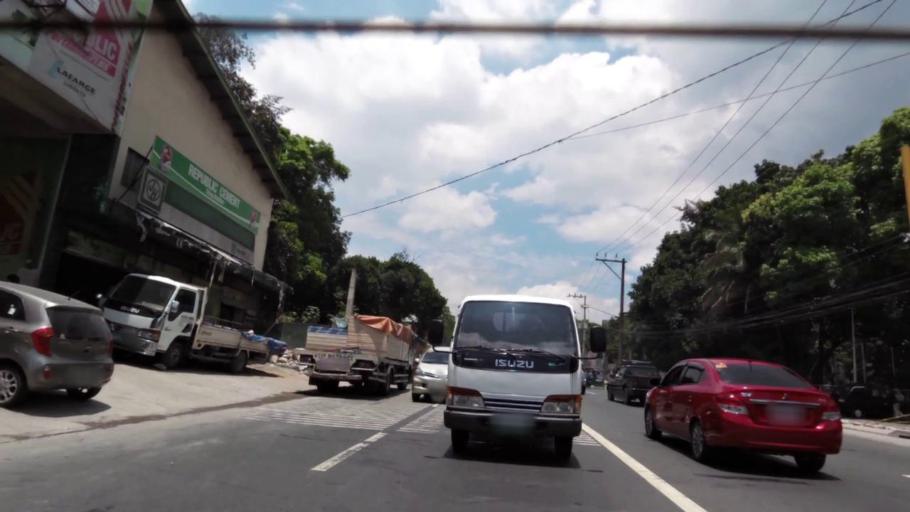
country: PH
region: Calabarzon
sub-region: Province of Rizal
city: Antipolo
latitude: 14.6054
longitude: 121.1739
